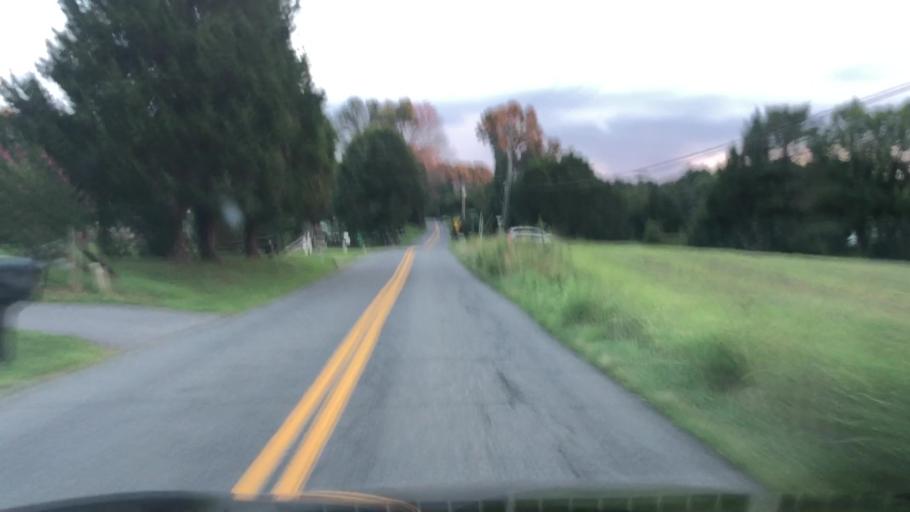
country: US
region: Virginia
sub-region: Stafford County
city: Stafford
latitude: 38.4771
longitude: -77.5801
